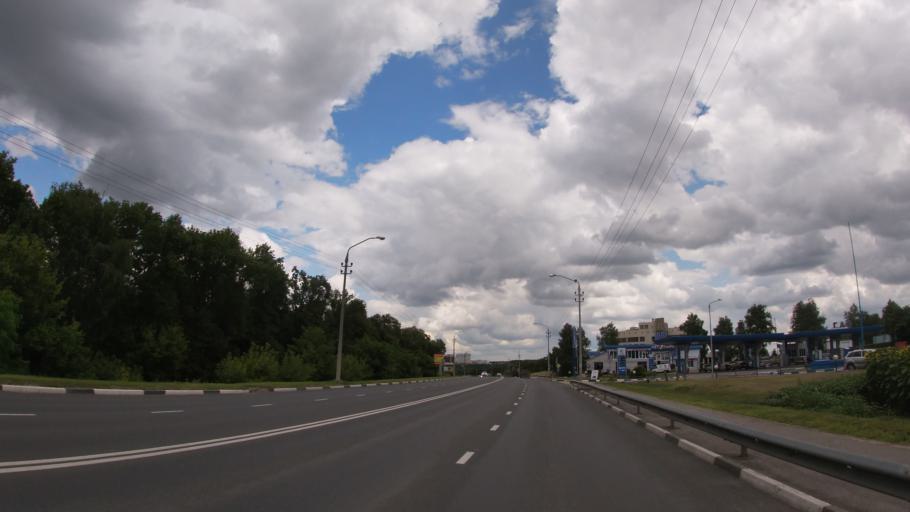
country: RU
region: Belgorod
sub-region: Belgorodskiy Rayon
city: Belgorod
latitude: 50.5531
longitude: 36.5796
